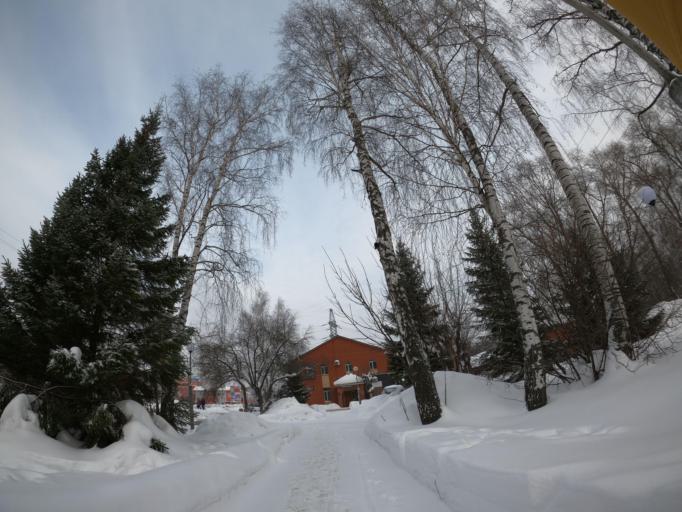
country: RU
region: Moskovskaya
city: Elektrogorsk
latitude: 55.8836
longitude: 38.7858
